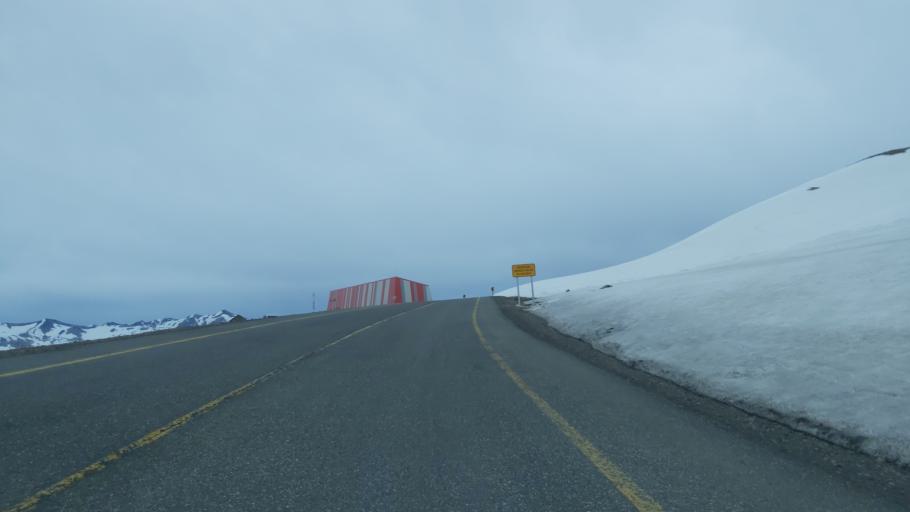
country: CL
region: Maule
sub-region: Provincia de Linares
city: Colbun
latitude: -36.0080
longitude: -70.4806
